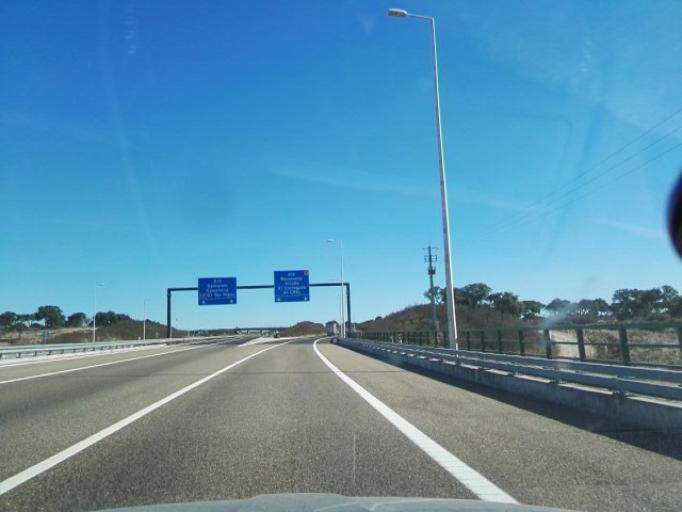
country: PT
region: Santarem
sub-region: Benavente
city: Poceirao
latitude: 38.8970
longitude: -8.7869
